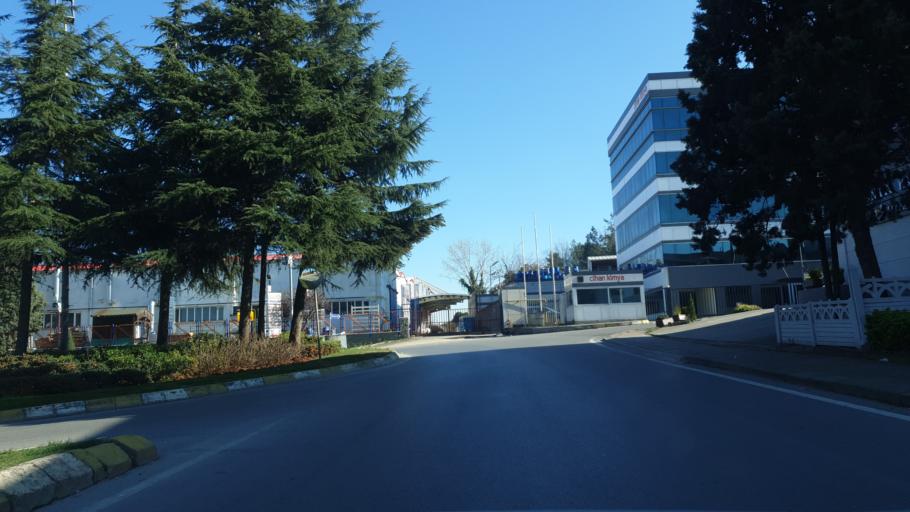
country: TR
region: Istanbul
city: Icmeler
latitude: 40.8788
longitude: 29.3512
